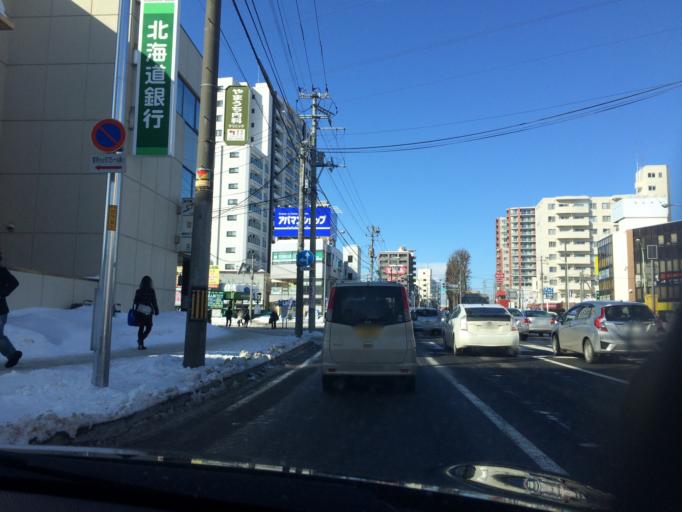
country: JP
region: Hokkaido
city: Sapporo
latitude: 43.0301
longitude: 141.4357
